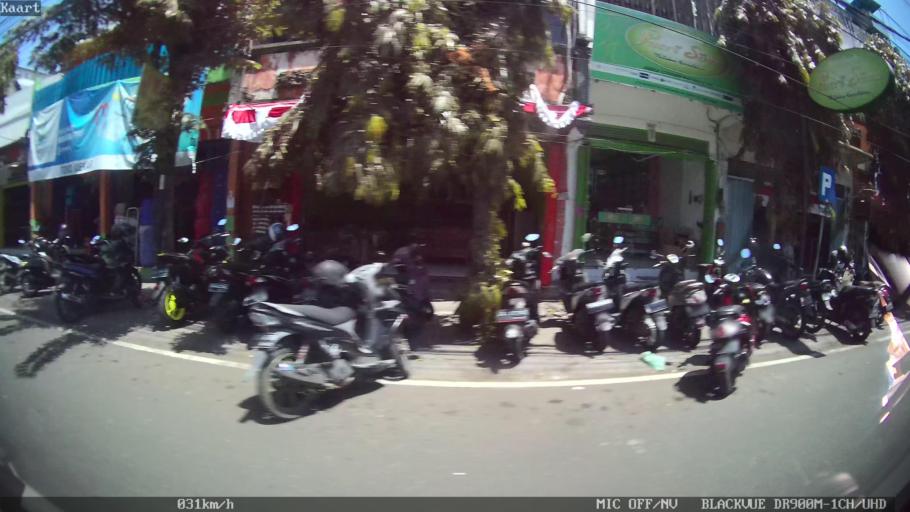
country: ID
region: Bali
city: Banjar Kampungkajanan
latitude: -8.1082
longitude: 115.0890
